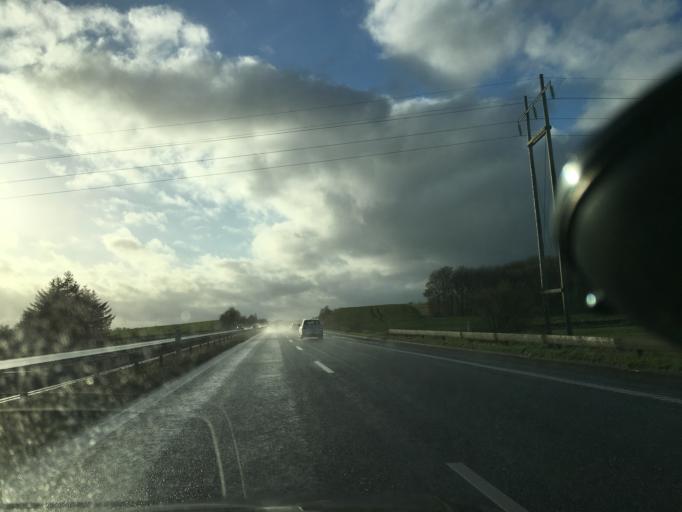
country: DK
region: North Denmark
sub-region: Mariagerfjord Kommune
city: Mariager
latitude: 56.5448
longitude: 9.8914
